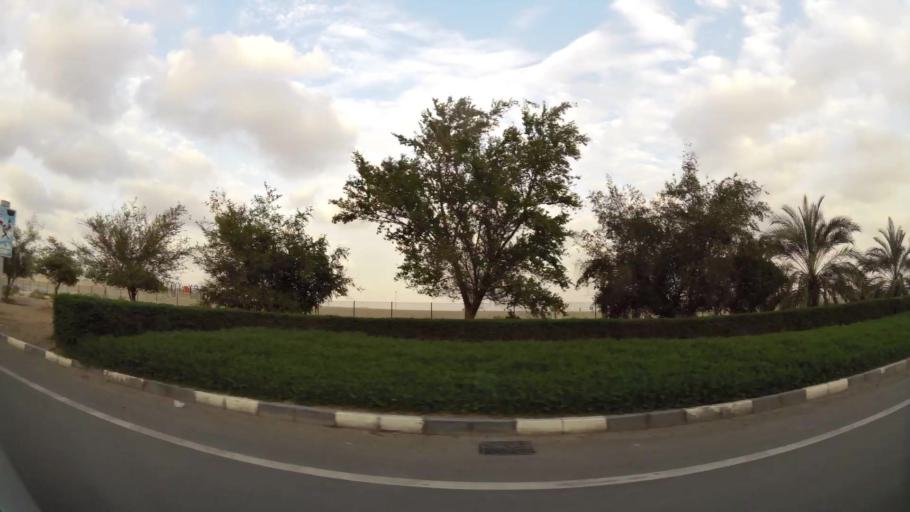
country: AE
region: Abu Dhabi
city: Abu Dhabi
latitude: 24.3615
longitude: 54.5257
